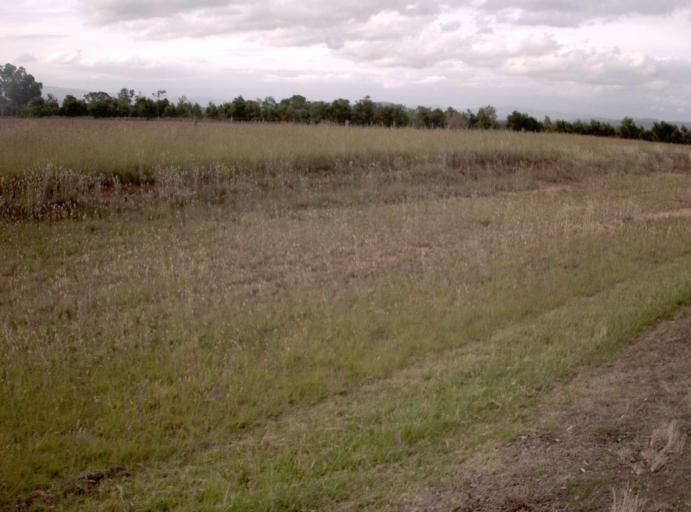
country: AU
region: Victoria
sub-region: Wellington
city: Sale
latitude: -37.8505
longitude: 147.0540
